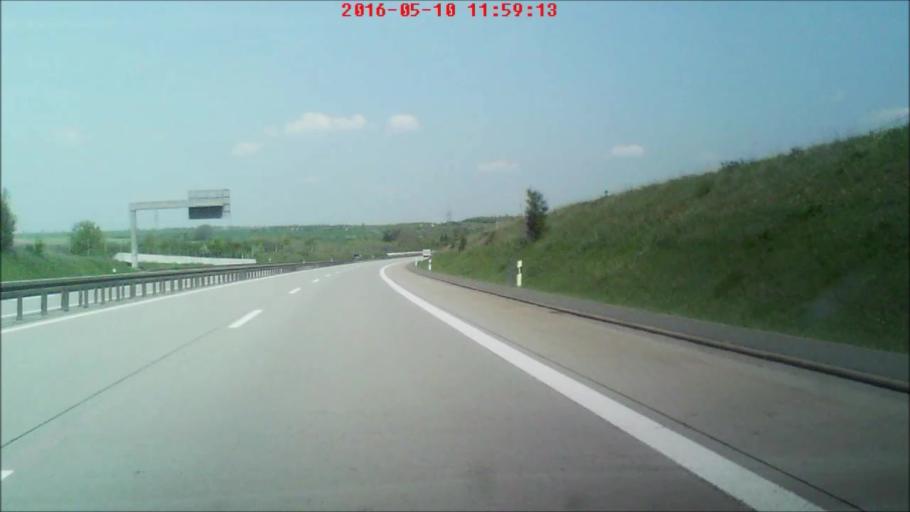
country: DE
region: Thuringia
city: Ingersleben
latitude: 50.9165
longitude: 10.9444
